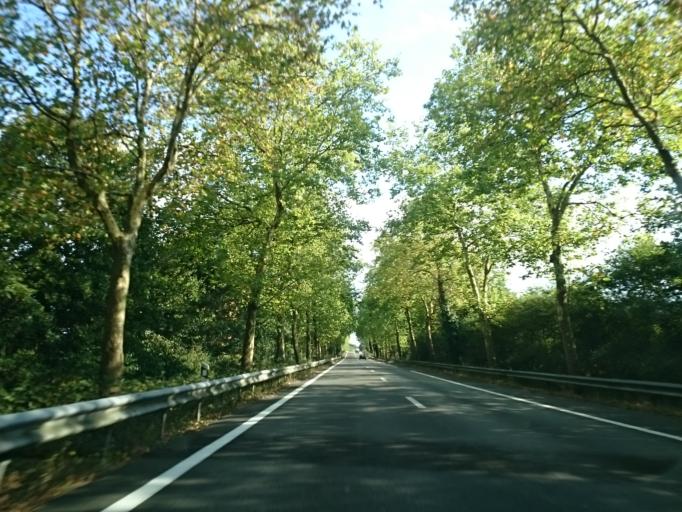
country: FR
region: Pays de la Loire
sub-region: Departement de la Loire-Atlantique
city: Heric
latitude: 47.3849
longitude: -1.6436
